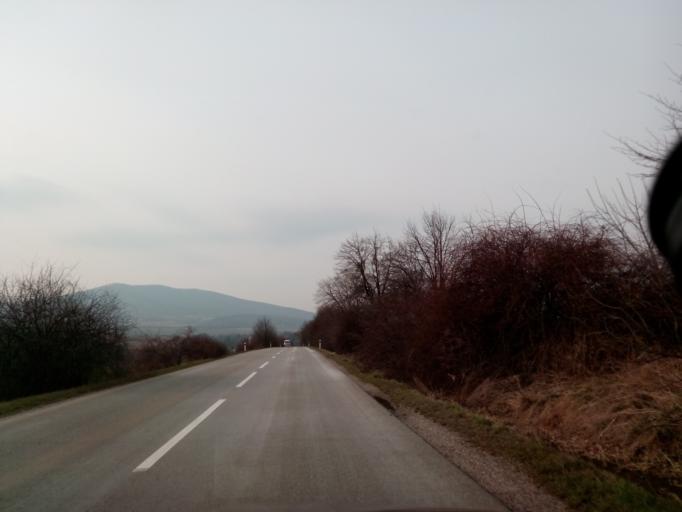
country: SK
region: Kosicky
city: Secovce
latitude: 48.6246
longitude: 21.5326
